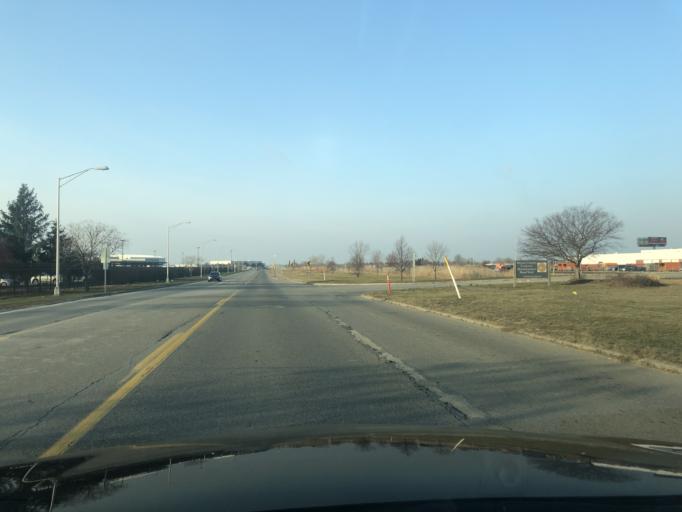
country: US
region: Michigan
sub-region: Wayne County
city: Inkster
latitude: 42.2386
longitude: -83.3321
